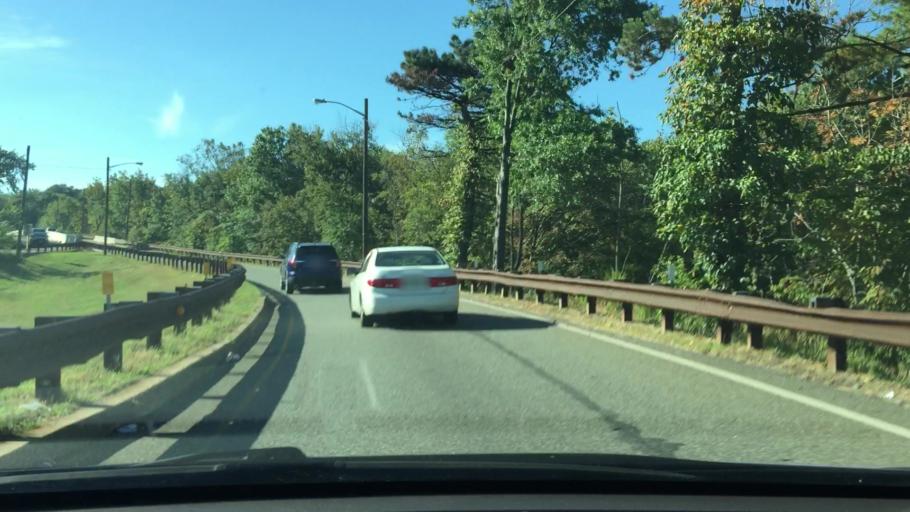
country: US
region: New Jersey
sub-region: Passaic County
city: Clifton
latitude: 40.8565
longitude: -74.1752
